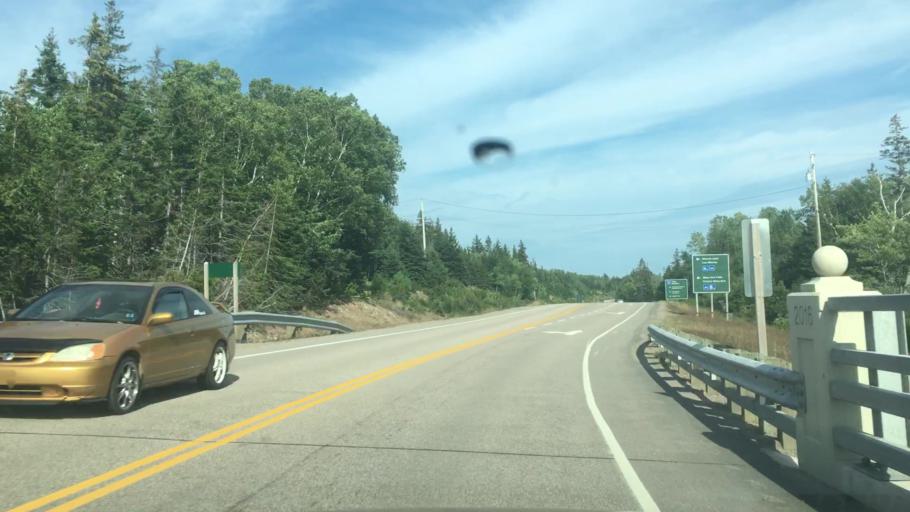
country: CA
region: Nova Scotia
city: Sydney Mines
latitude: 46.7122
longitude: -60.3667
